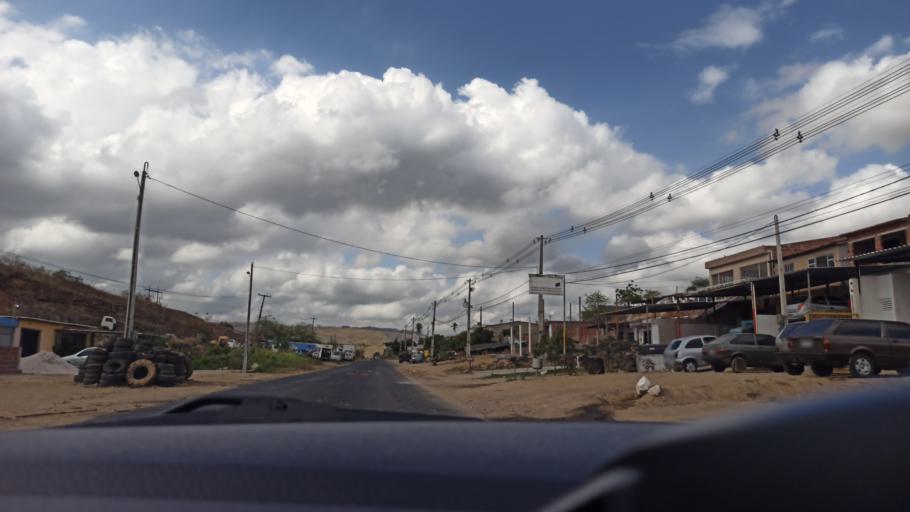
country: BR
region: Pernambuco
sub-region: Timbauba
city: Timbauba
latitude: -7.5042
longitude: -35.2994
